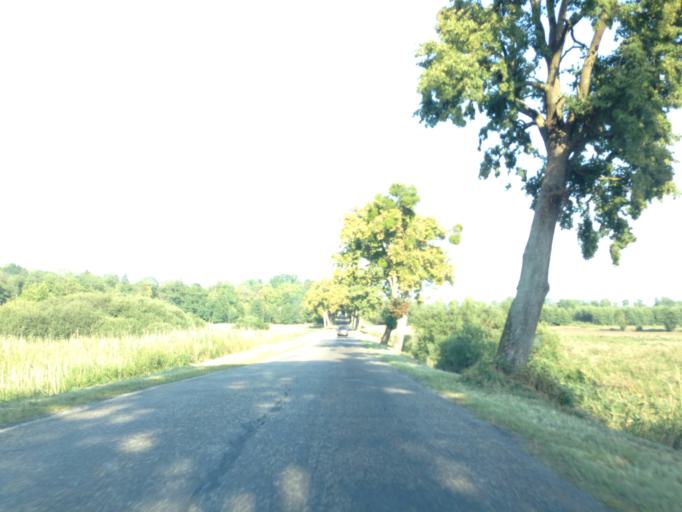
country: PL
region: Kujawsko-Pomorskie
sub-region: Powiat grudziadzki
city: Swiecie nad Osa
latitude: 53.4996
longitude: 19.2024
